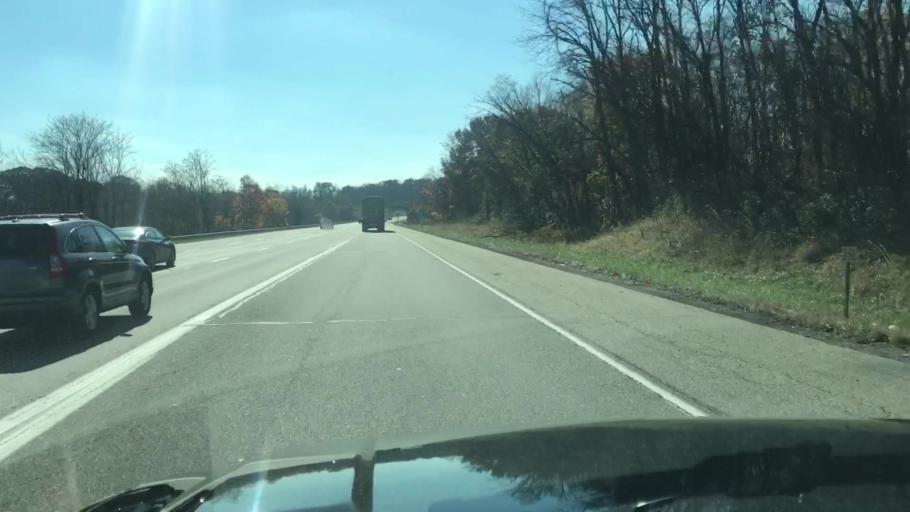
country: US
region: Pennsylvania
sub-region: Cumberland County
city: Enola
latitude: 40.2857
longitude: -76.9833
